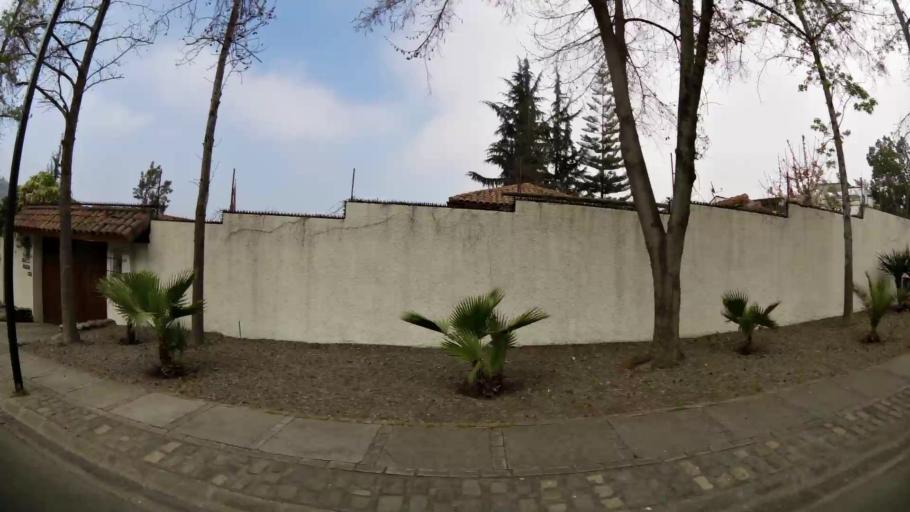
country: CL
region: Santiago Metropolitan
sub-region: Provincia de Santiago
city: Villa Presidente Frei, Nunoa, Santiago, Chile
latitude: -33.3668
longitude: -70.5745
